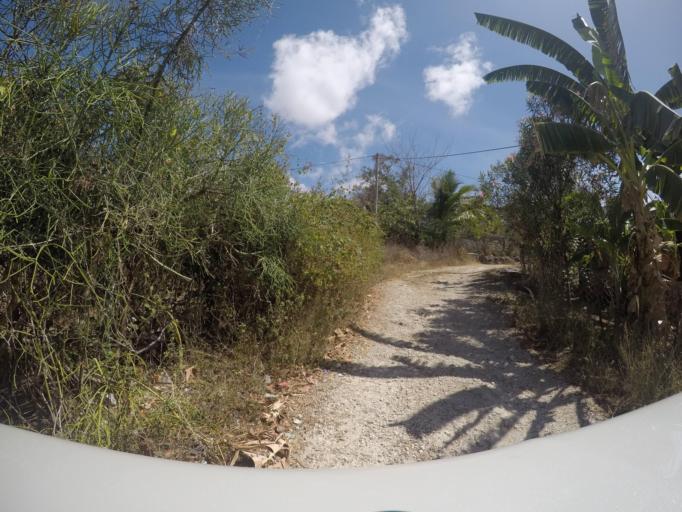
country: TL
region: Baucau
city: Baucau
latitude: -8.4451
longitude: 126.4401
